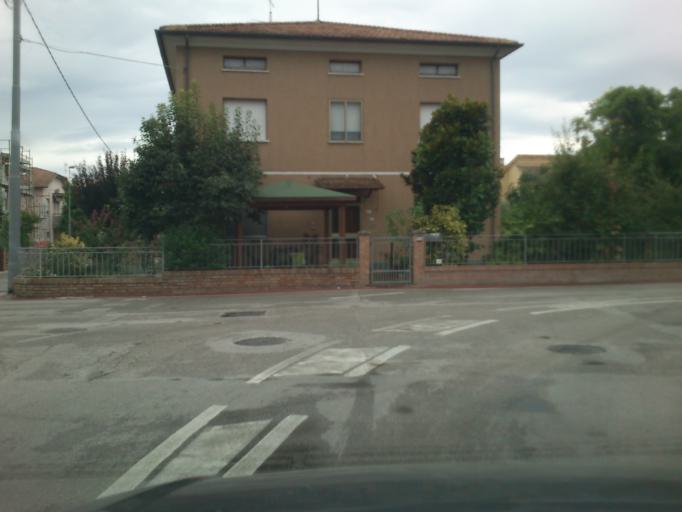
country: IT
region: The Marches
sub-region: Provincia di Pesaro e Urbino
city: Lucrezia
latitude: 43.7713
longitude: 12.9363
